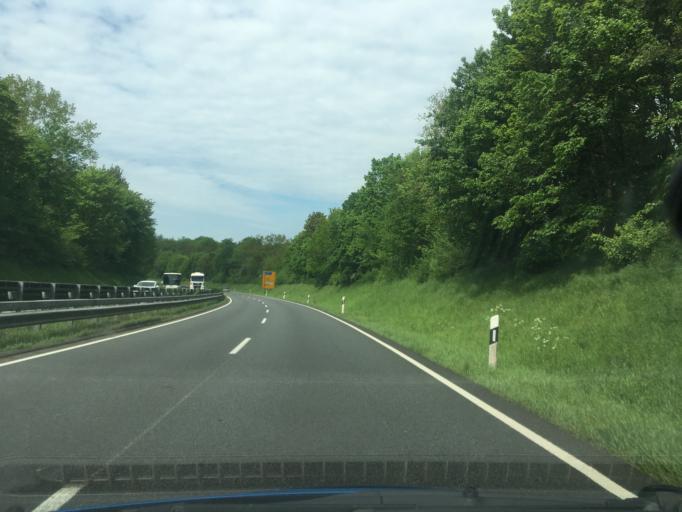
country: DE
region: Lower Saxony
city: Adendorf
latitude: 53.2662
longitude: 10.4409
